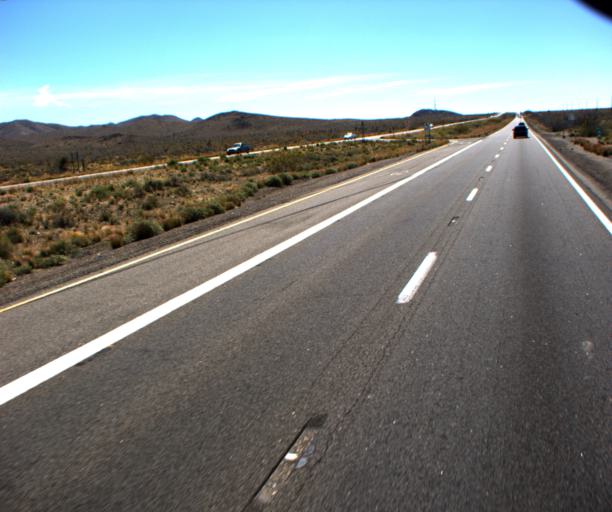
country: US
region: Arizona
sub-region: Mohave County
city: Dolan Springs
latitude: 35.4567
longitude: -114.3022
